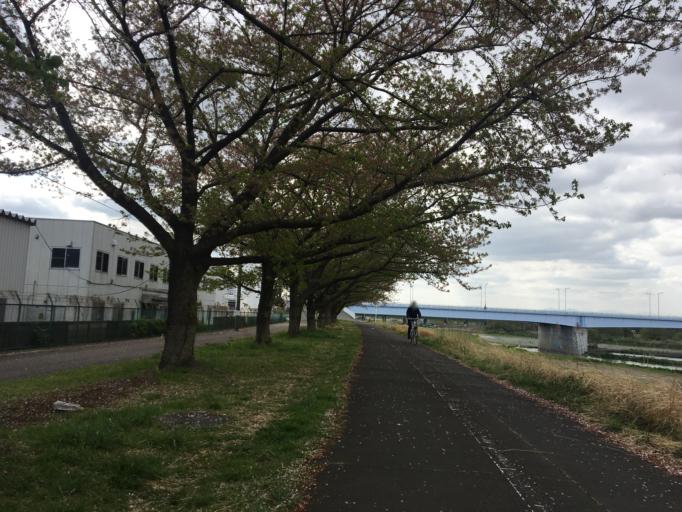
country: JP
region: Tokyo
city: Kokubunji
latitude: 35.6519
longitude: 139.4906
